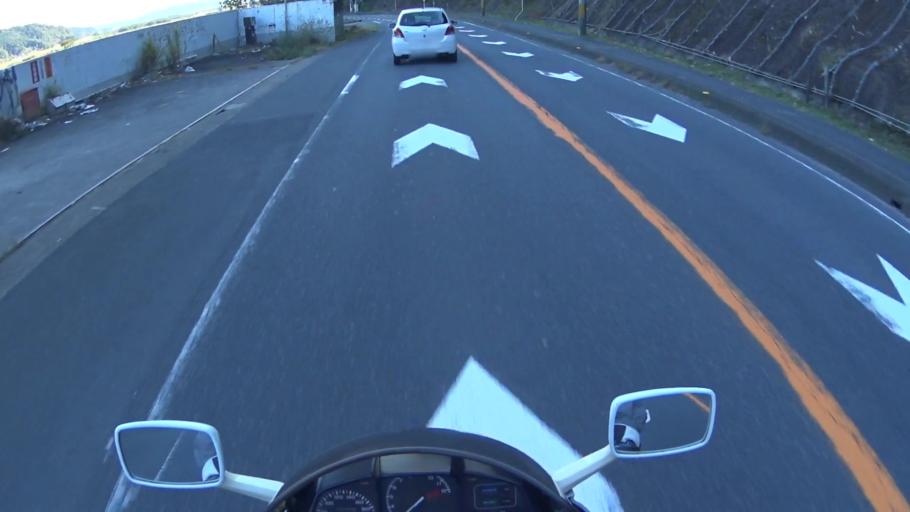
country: JP
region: Kyoto
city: Fukuchiyama
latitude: 35.3471
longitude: 135.1075
